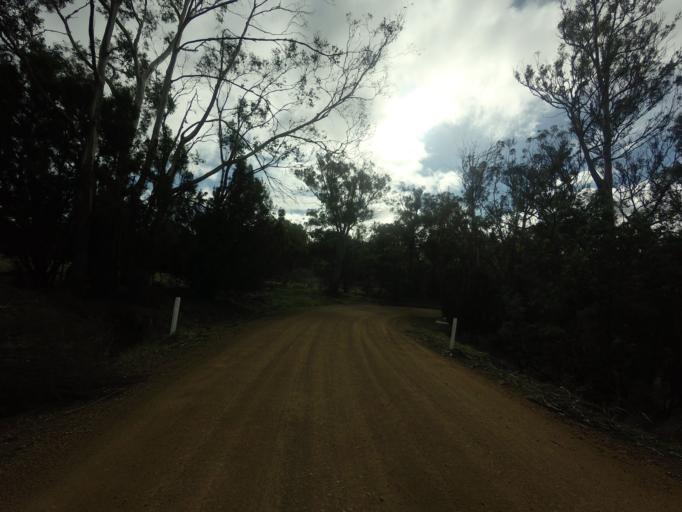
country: AU
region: Tasmania
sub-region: Derwent Valley
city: New Norfolk
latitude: -42.7264
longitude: 146.8669
